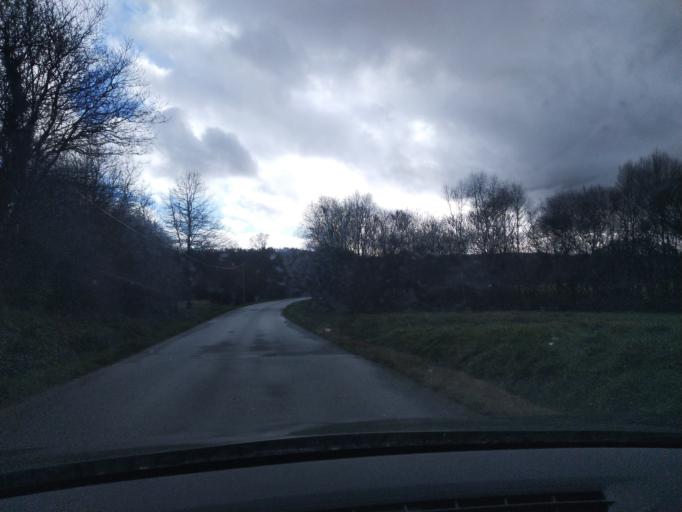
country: FR
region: Brittany
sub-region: Departement du Finistere
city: Guerlesquin
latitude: 48.5078
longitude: -3.5882
